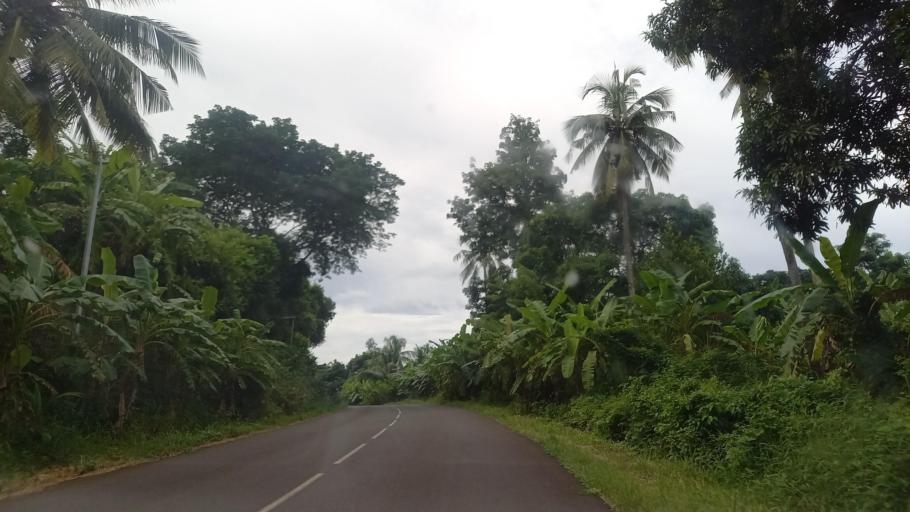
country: YT
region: Boueni
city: Boueni
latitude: -12.9128
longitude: 45.1013
